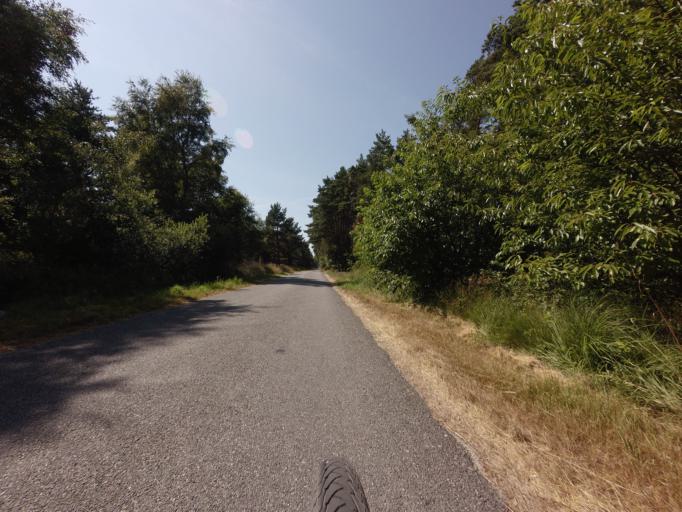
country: DK
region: North Denmark
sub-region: Laeso Kommune
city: Byrum
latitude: 57.2906
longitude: 10.9624
